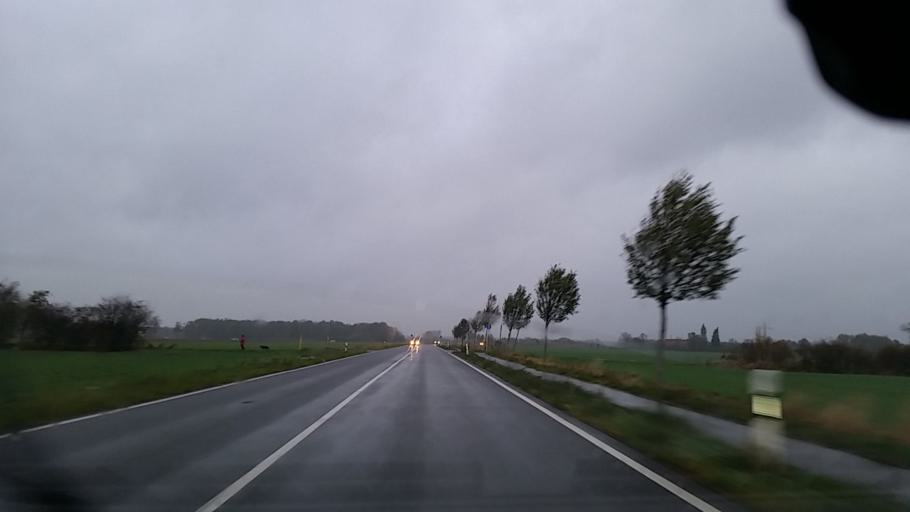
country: DE
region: Lower Saxony
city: Calberlah
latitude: 52.4123
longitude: 10.6716
